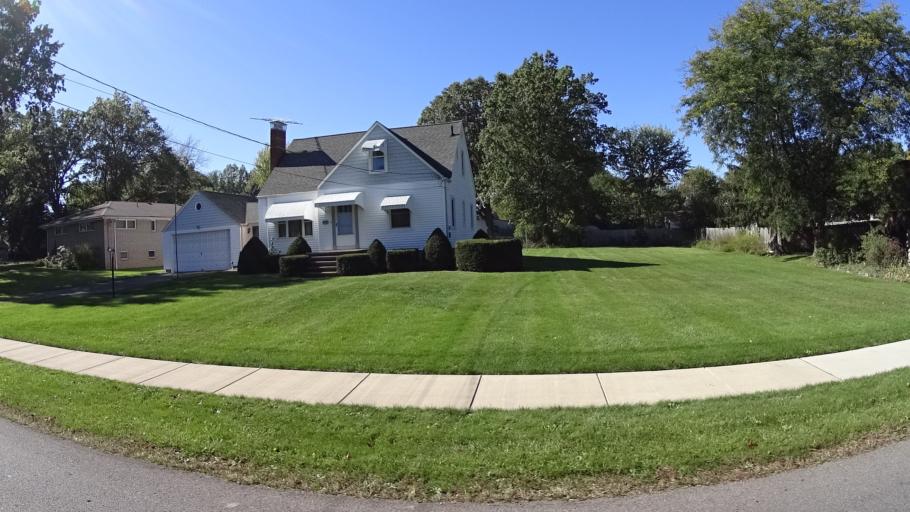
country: US
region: Ohio
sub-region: Lorain County
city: Lorain
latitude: 41.4275
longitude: -82.1582
